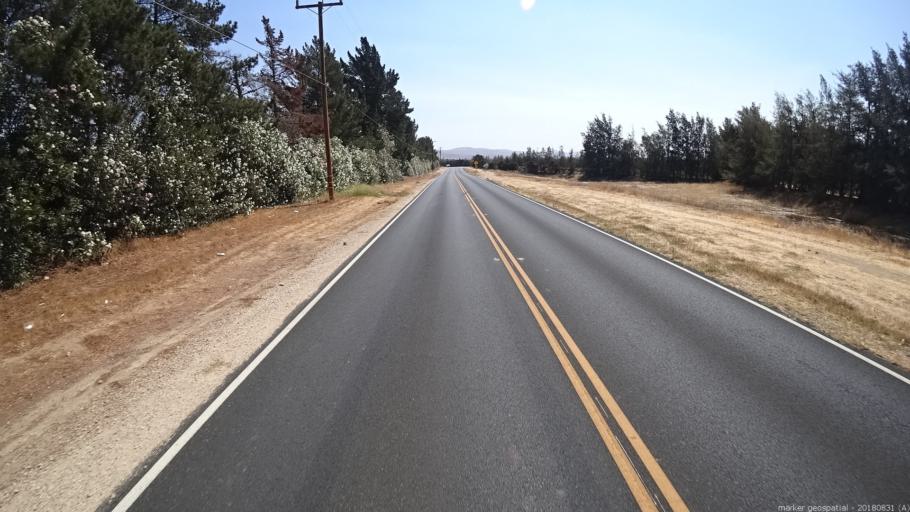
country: US
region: California
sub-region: Monterey County
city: Soledad
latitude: 36.4237
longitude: -121.2983
